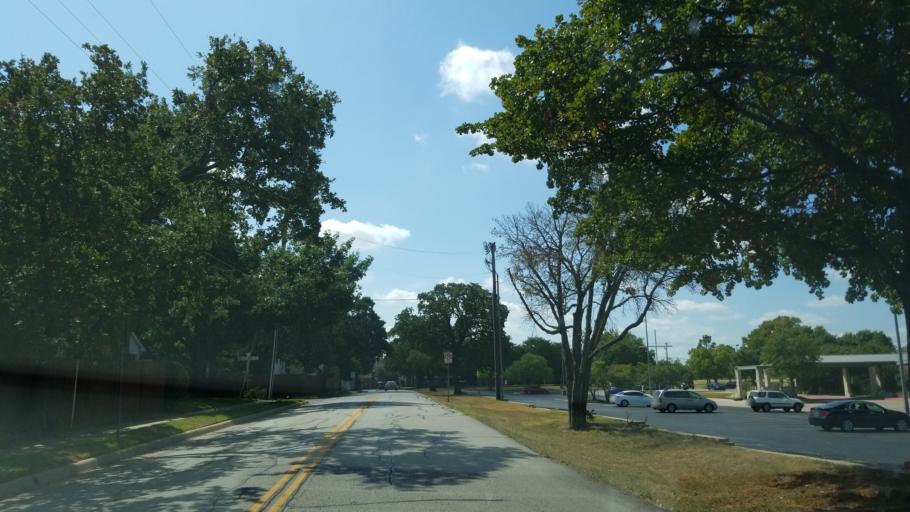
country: US
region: Texas
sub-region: Tarrant County
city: Euless
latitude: 32.8536
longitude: -97.1043
